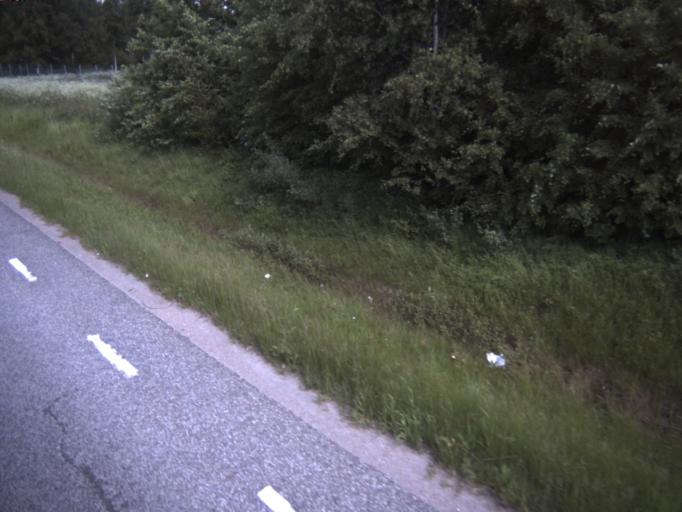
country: SE
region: Skane
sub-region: Helsingborg
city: Odakra
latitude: 56.0768
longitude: 12.7632
